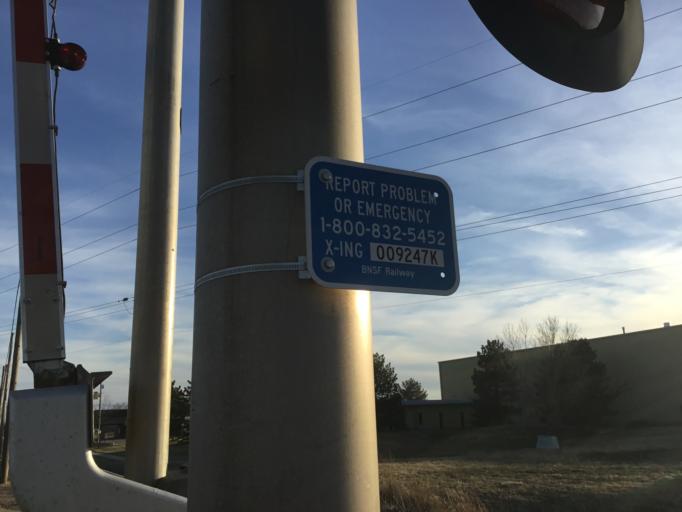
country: US
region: Kansas
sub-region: Sedgwick County
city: Valley Center
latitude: 37.8268
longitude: -97.3721
